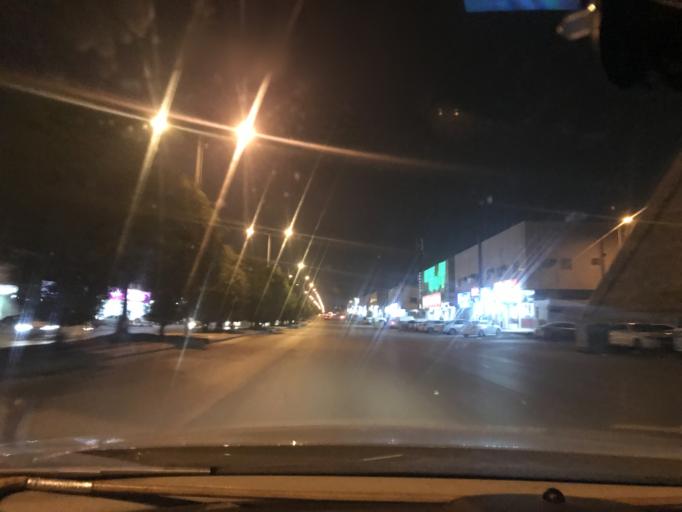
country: SA
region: Ar Riyad
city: Riyadh
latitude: 24.7544
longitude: 46.7467
